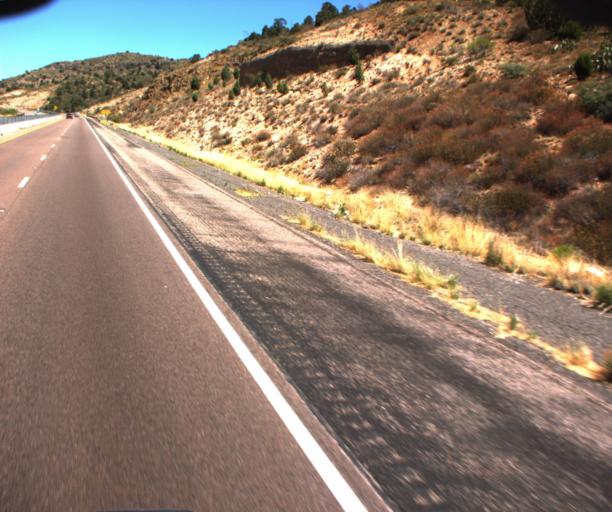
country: US
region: Arizona
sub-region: Gila County
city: Tonto Basin
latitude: 33.9098
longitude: -111.4505
